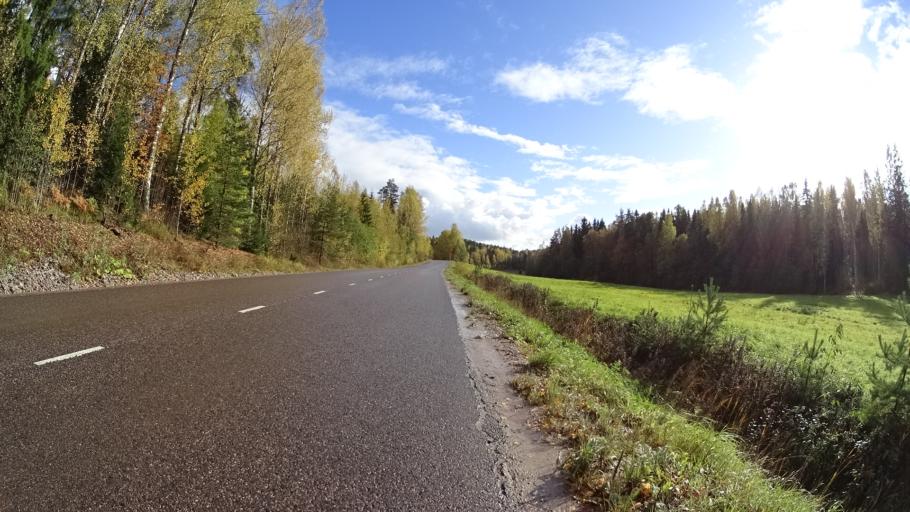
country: FI
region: Uusimaa
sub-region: Helsinki
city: Kilo
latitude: 60.2919
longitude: 24.8018
